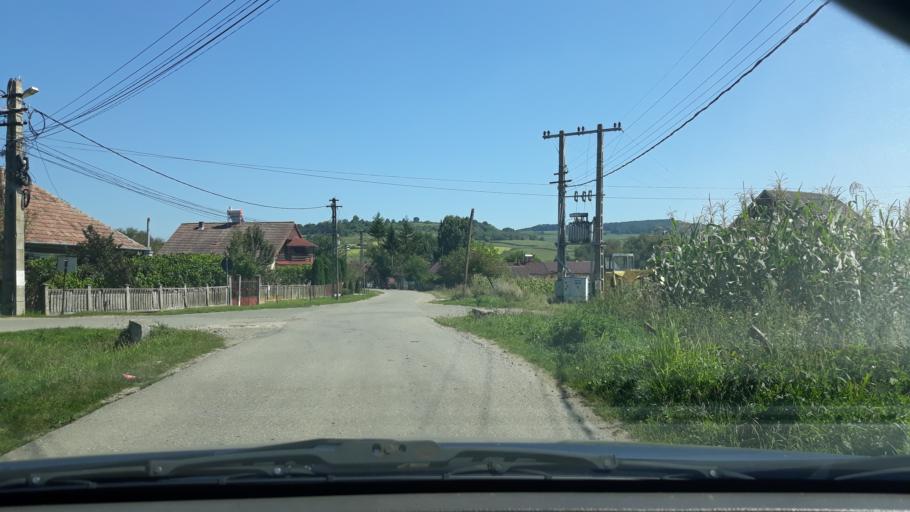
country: RO
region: Salaj
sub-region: Comuna Dobrin
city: Dobrin
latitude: 47.2892
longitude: 23.0949
